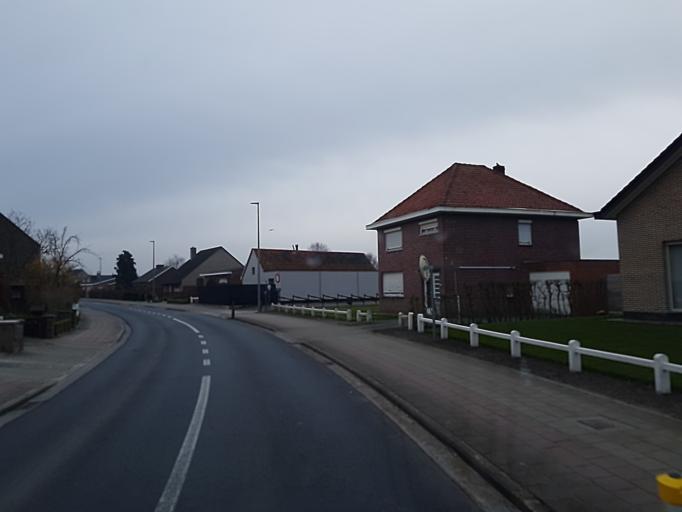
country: BE
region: Flanders
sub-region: Provincie Oost-Vlaanderen
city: Waarschoot
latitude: 51.1611
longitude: 3.6154
